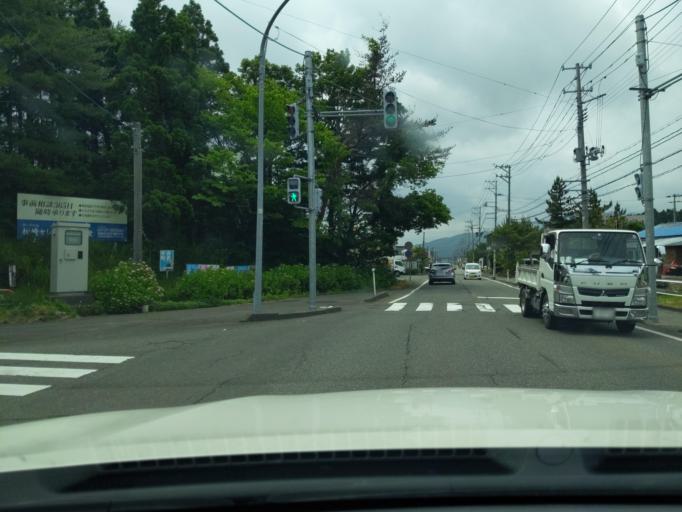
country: JP
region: Niigata
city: Kashiwazaki
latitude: 37.3496
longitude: 138.5702
